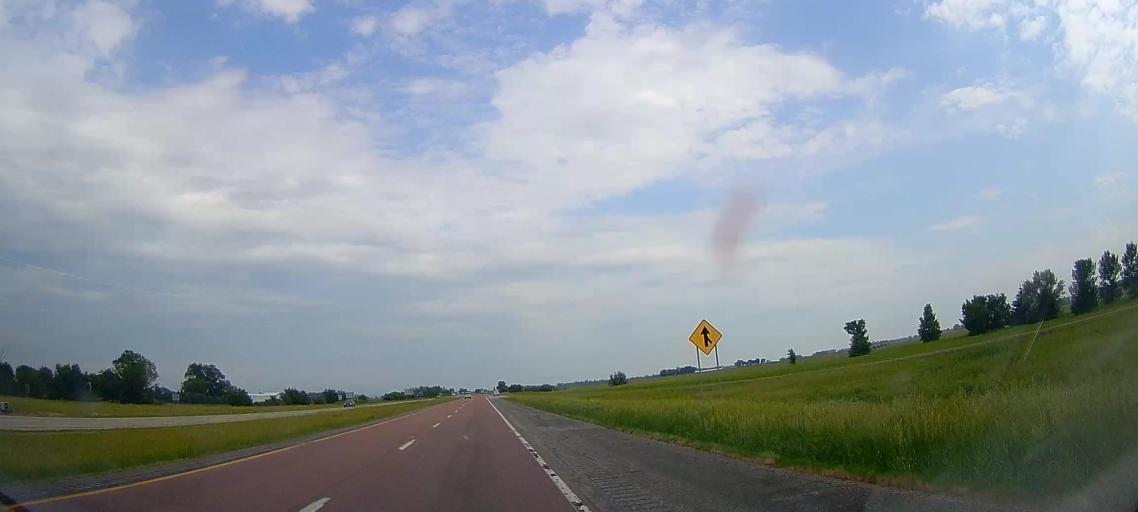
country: US
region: Iowa
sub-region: Monona County
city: Onawa
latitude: 42.0246
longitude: -96.1308
